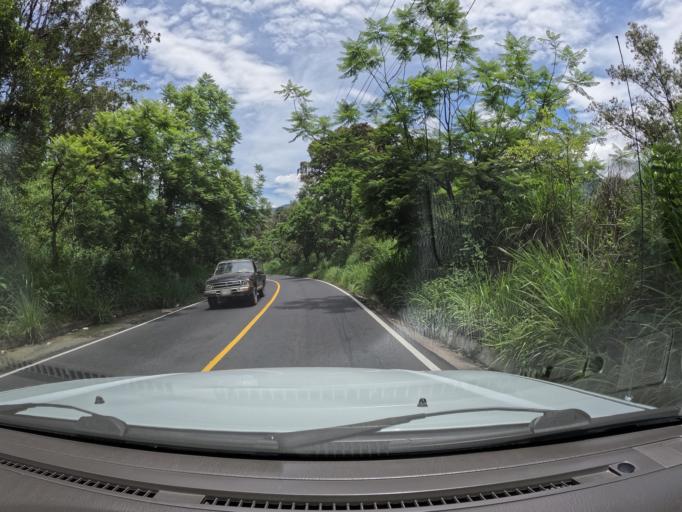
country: GT
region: Guatemala
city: Amatitlan
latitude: 14.5003
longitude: -90.6257
